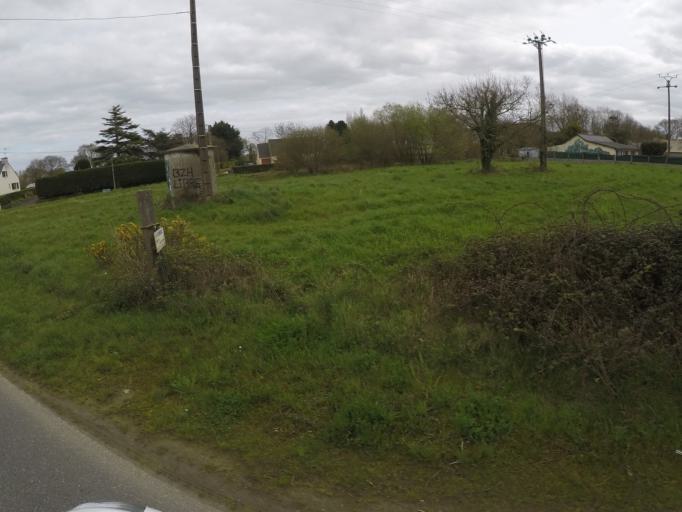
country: FR
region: Brittany
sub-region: Departement des Cotes-d'Armor
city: Plouha
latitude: 48.6656
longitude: -2.9486
